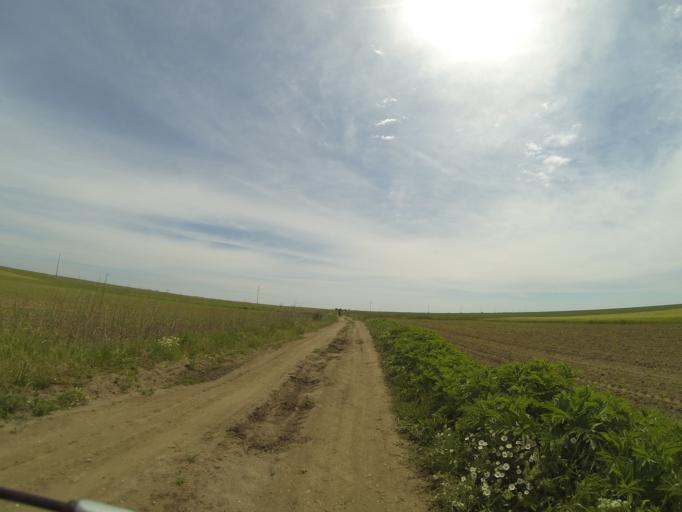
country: RO
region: Dolj
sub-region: Comuna Ghindeni
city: Ghindeni
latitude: 44.2072
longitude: 23.9429
